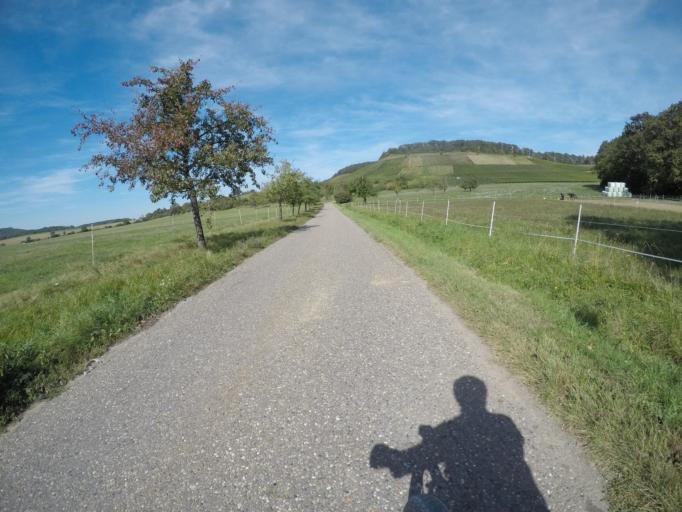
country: DE
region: Baden-Wuerttemberg
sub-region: Karlsruhe Region
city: Sternenfels
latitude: 49.0179
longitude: 8.8715
